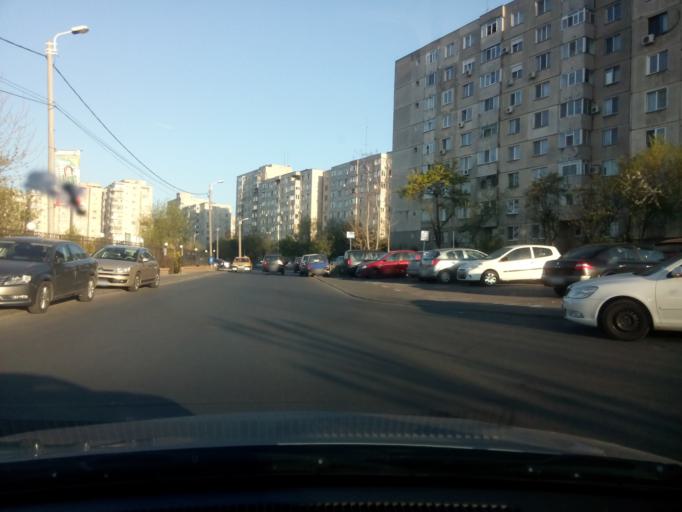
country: RO
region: Ilfov
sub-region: Comuna Fundeni-Dobroesti
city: Fundeni
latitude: 44.4451
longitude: 26.1604
